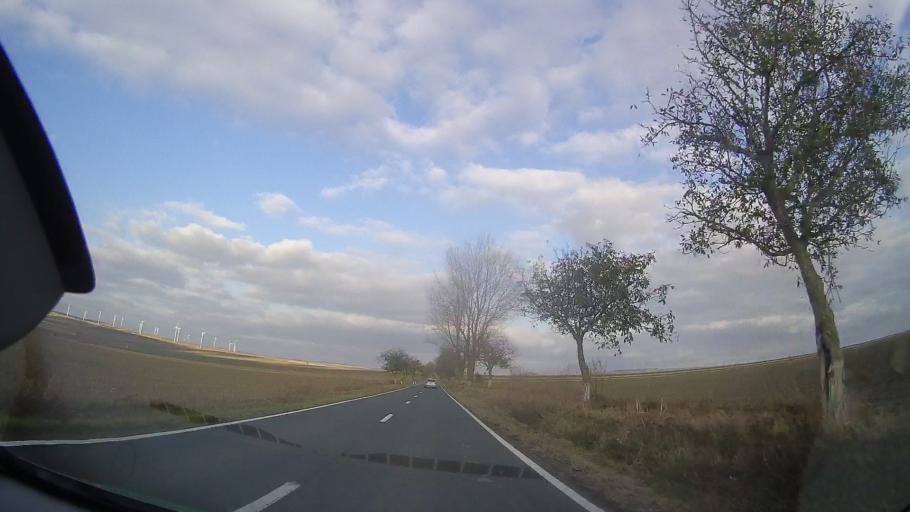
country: RO
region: Tulcea
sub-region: Comuna Topolog
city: Topolog
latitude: 44.8575
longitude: 28.3387
